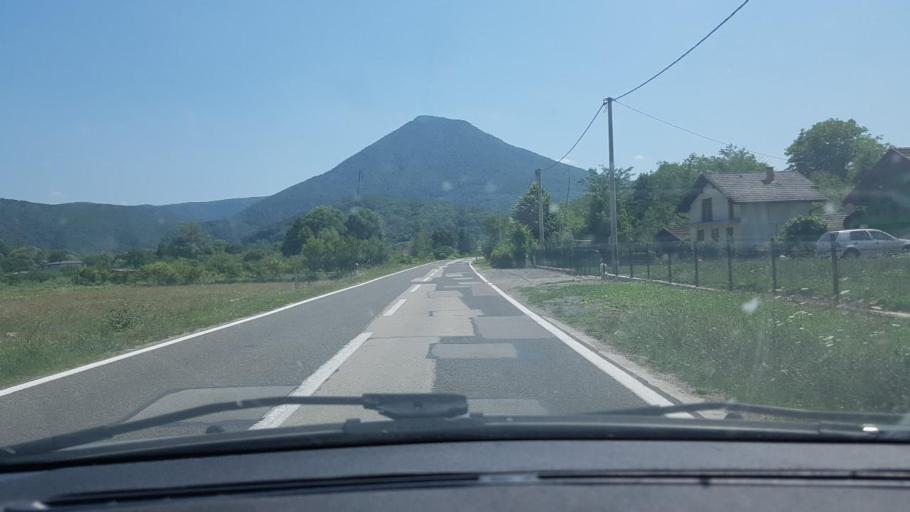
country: BA
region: Federation of Bosnia and Herzegovina
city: Bihac
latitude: 44.7588
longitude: 15.9448
